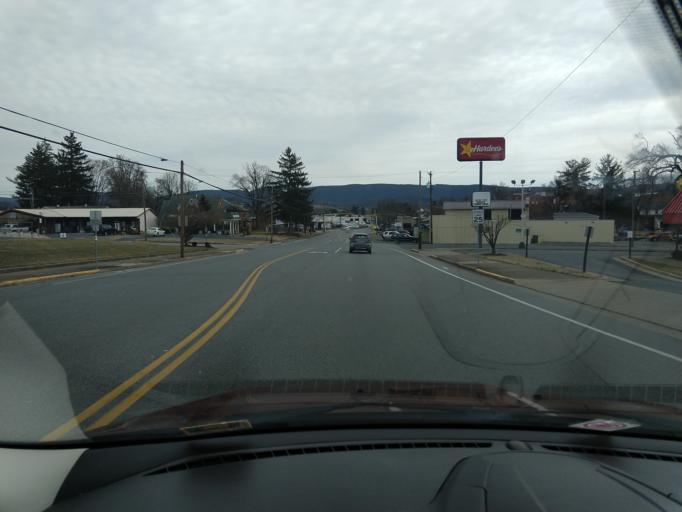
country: US
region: Virginia
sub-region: City of Waynesboro
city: Waynesboro
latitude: 38.0723
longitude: -78.9004
